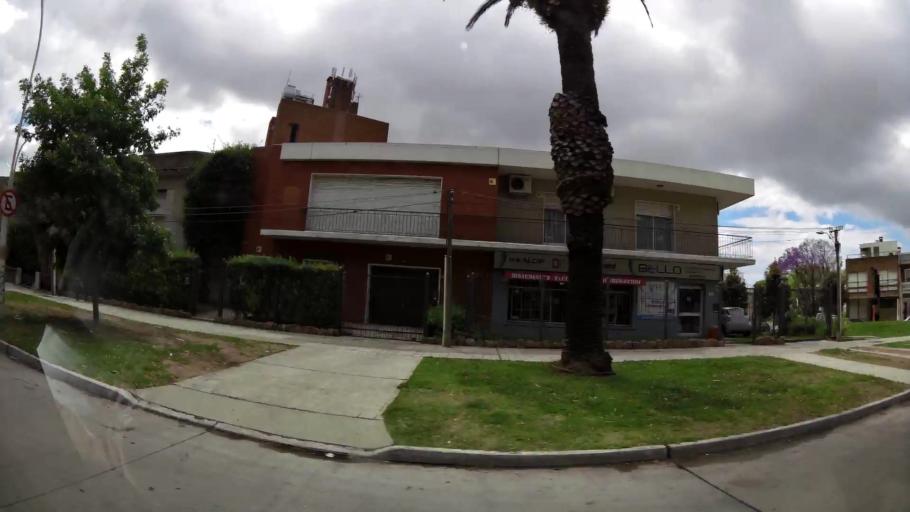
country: UY
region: Montevideo
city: Montevideo
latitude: -34.8829
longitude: -56.1663
